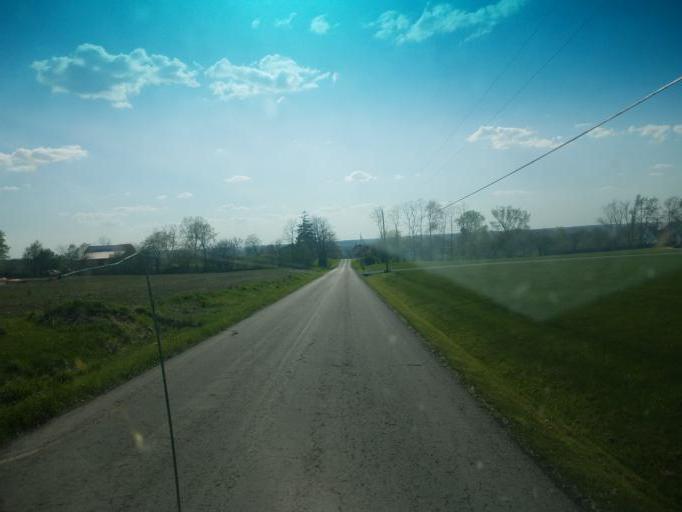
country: US
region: Ohio
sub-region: Wayne County
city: Wooster
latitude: 40.7481
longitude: -81.9132
